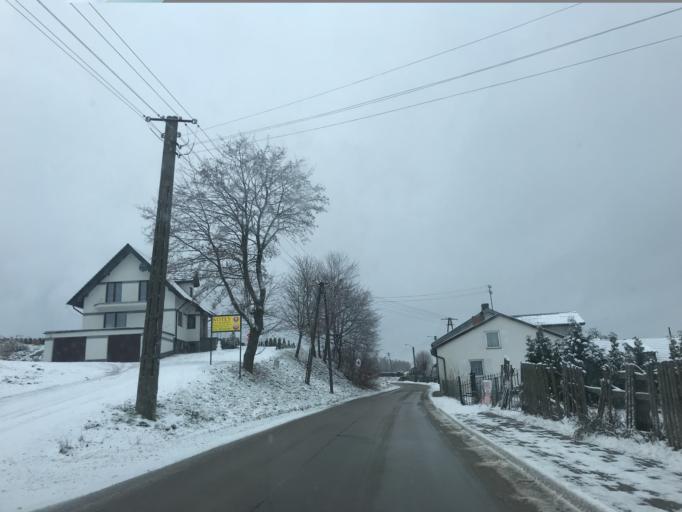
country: PL
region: Pomeranian Voivodeship
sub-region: Powiat bytowski
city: Bytow
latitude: 54.2179
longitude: 17.5621
